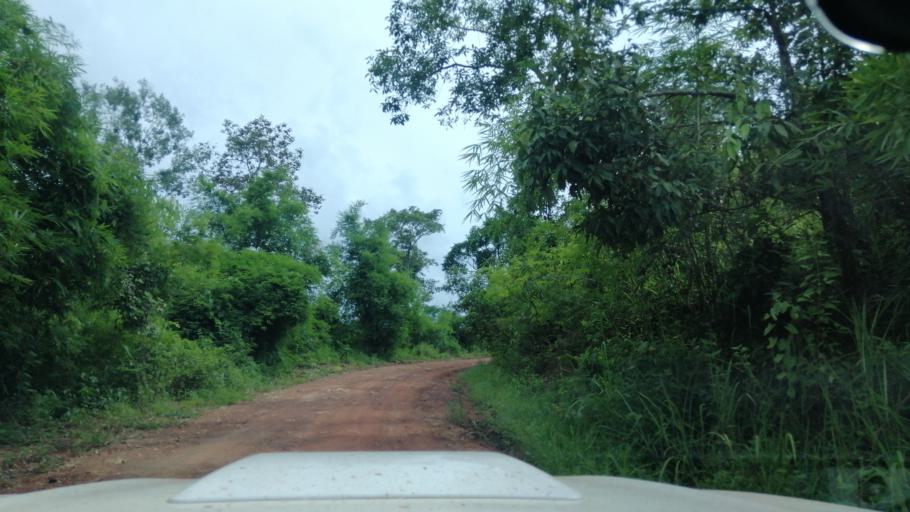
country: TH
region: Nan
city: Mae Charim
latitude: 18.7861
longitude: 101.3235
